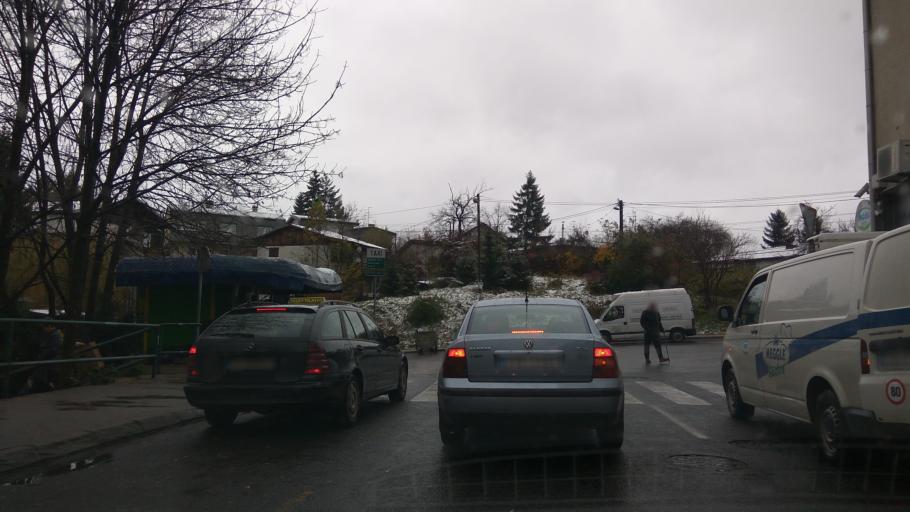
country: BA
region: Federation of Bosnia and Herzegovina
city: Kobilja Glava
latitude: 43.8697
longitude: 18.4066
